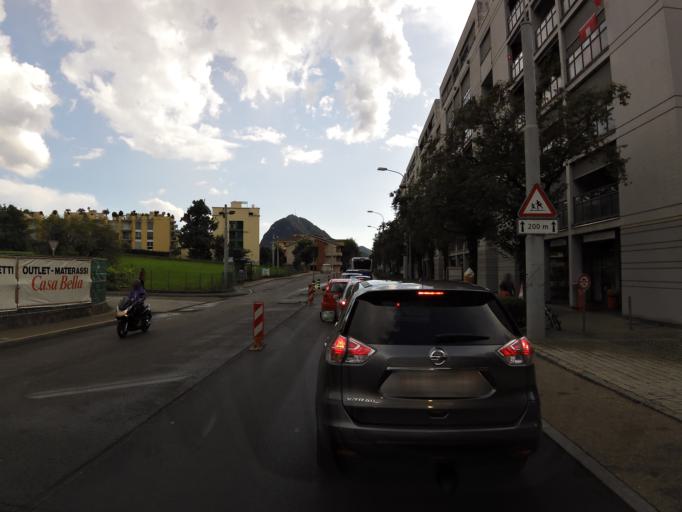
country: CH
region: Ticino
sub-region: Lugano District
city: Viganello
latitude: 46.0213
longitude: 8.9659
